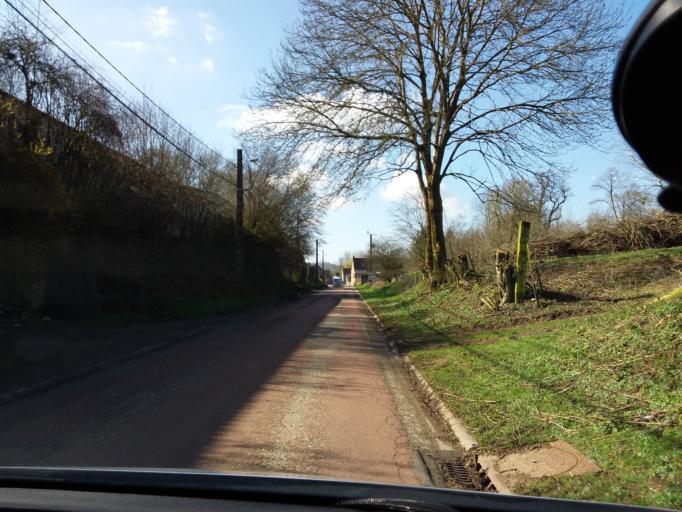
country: FR
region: Picardie
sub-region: Departement de l'Aisne
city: Hirson
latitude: 49.8806
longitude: 4.0965
